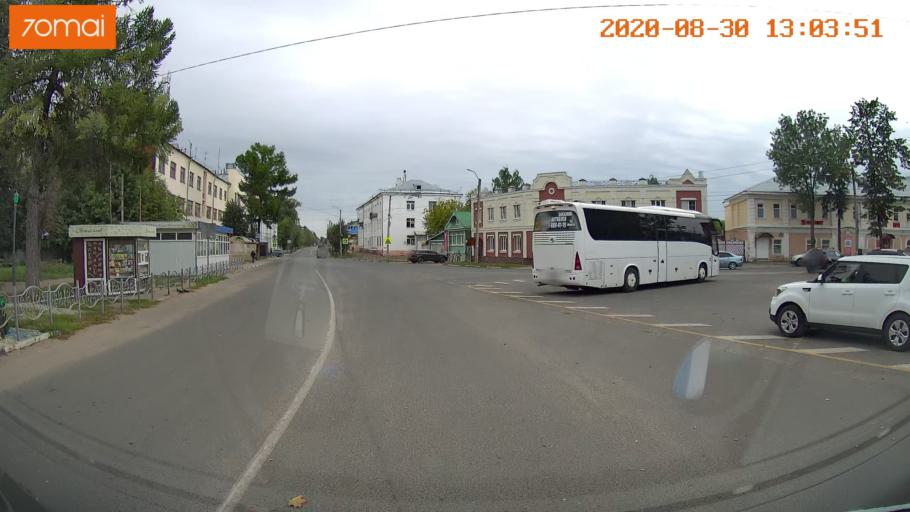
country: RU
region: Ivanovo
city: Kineshma
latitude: 57.4451
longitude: 42.1559
